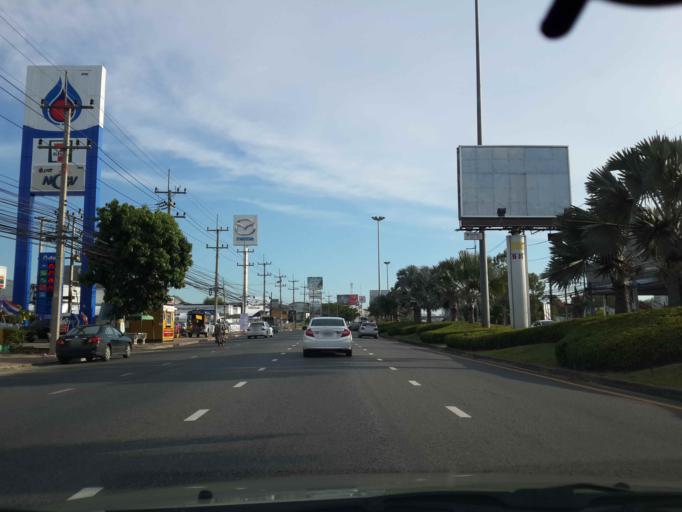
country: TH
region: Chon Buri
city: Bang Lamung
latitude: 12.9895
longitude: 100.9247
